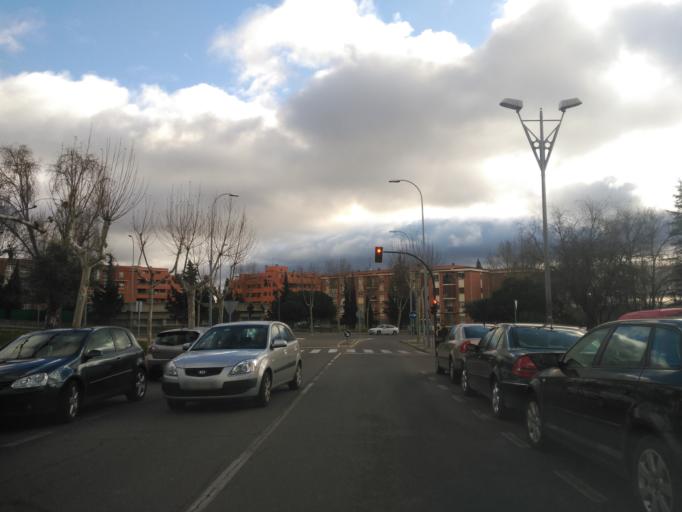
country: ES
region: Castille and Leon
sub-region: Provincia de Zamora
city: Zamora
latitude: 41.5062
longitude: -5.7334
